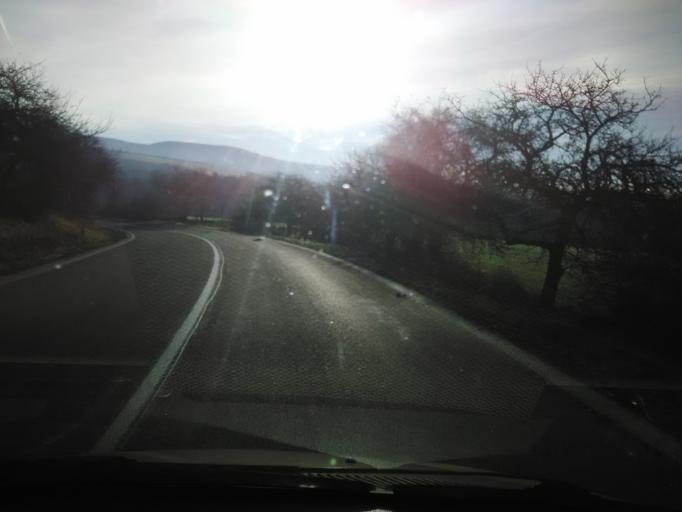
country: SK
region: Nitriansky
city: Tlmace
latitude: 48.3450
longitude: 18.5419
